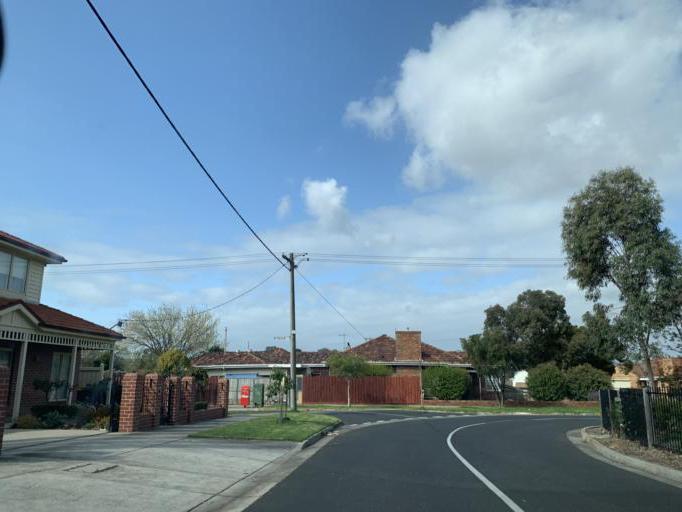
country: AU
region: Victoria
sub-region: Moreland
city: Pascoe Vale
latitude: -37.7402
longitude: 144.9355
